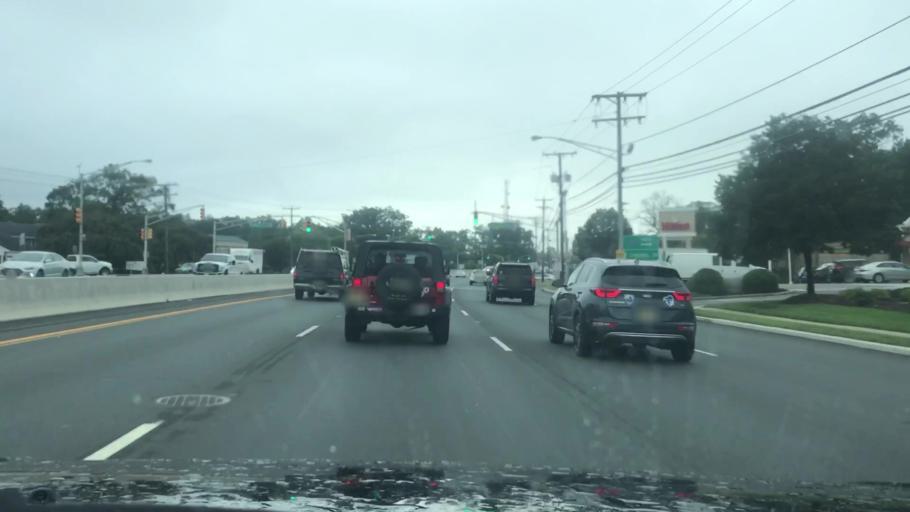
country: US
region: New Jersey
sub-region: Ocean County
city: Silver Ridge
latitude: 39.9673
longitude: -74.2278
